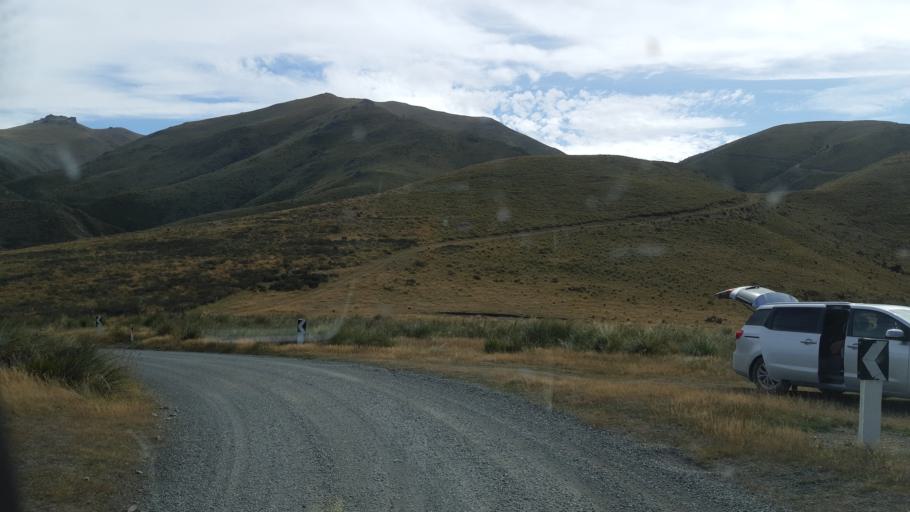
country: NZ
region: Canterbury
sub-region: Timaru District
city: Pleasant Point
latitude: -44.1932
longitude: 170.6099
